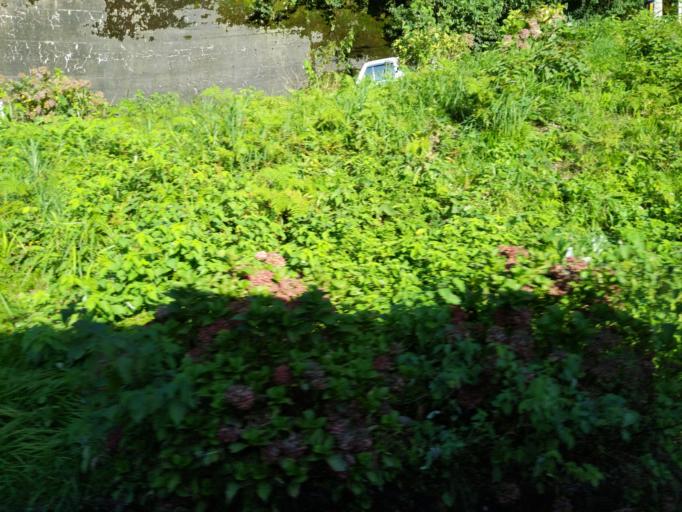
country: JP
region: Toyama
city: Kamiichi
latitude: 36.5699
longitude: 137.3845
